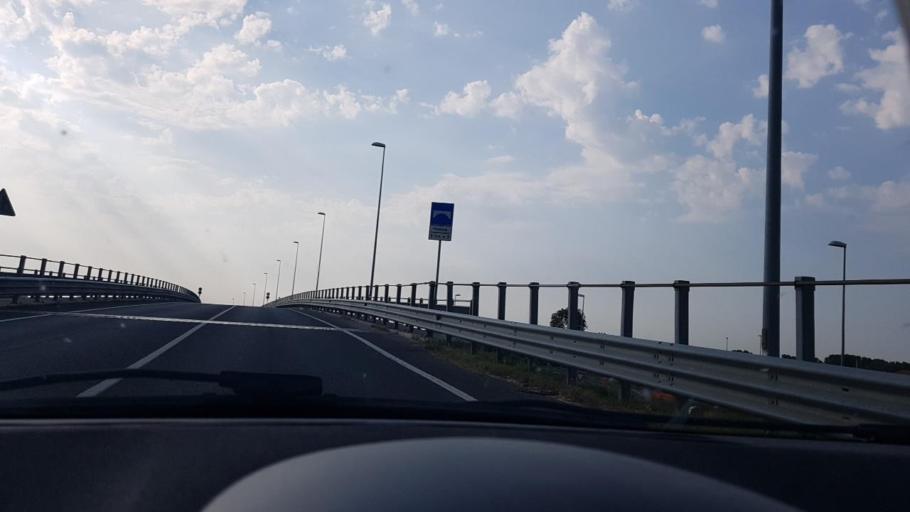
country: IT
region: Friuli Venezia Giulia
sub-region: Provincia di Pordenone
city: Pordenone
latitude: 45.9486
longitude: 12.6929
